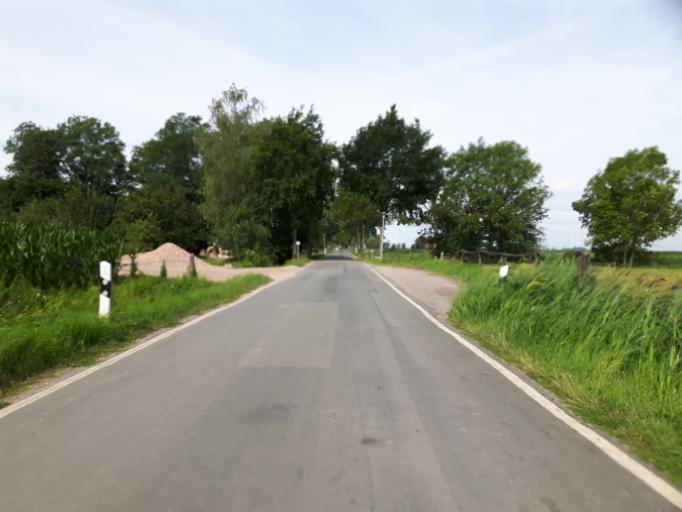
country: DE
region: Lower Saxony
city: Elsfleth
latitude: 53.2576
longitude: 8.4511
